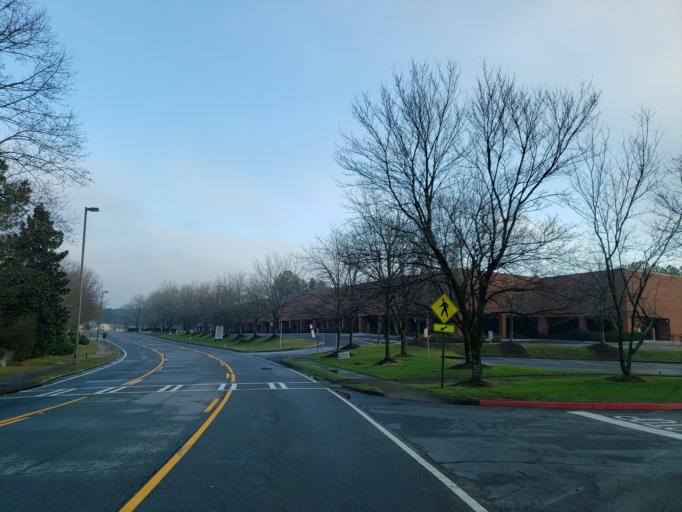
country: US
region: Georgia
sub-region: Cobb County
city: Kennesaw
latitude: 34.0071
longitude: -84.5962
